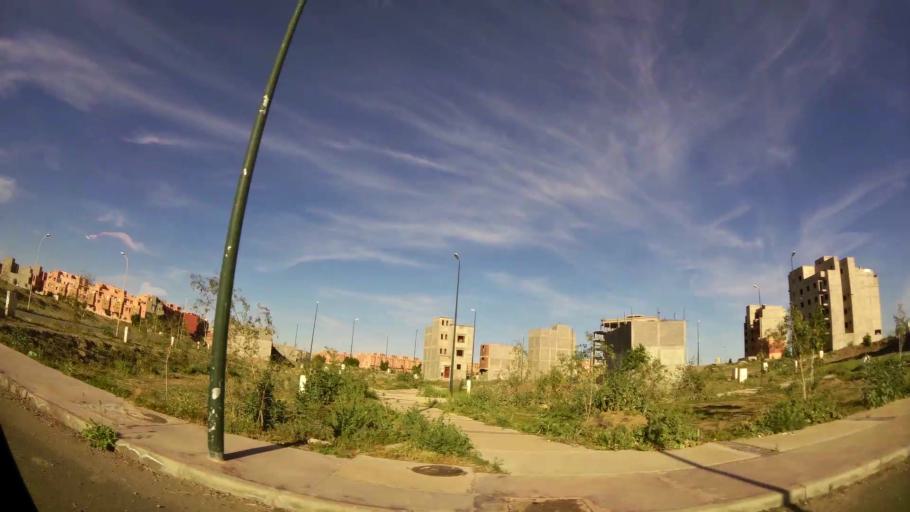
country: MA
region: Marrakech-Tensift-Al Haouz
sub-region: Marrakech
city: Marrakesh
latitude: 31.7551
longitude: -8.1028
